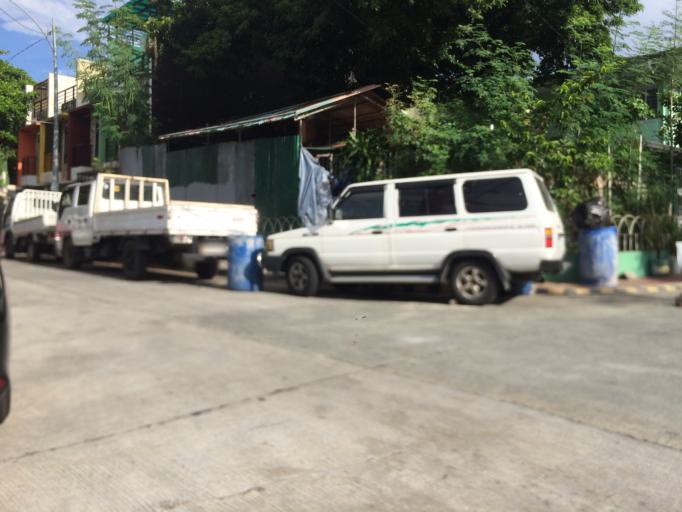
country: PH
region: Calabarzon
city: Bagong Pagasa
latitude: 14.6712
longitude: 121.0227
